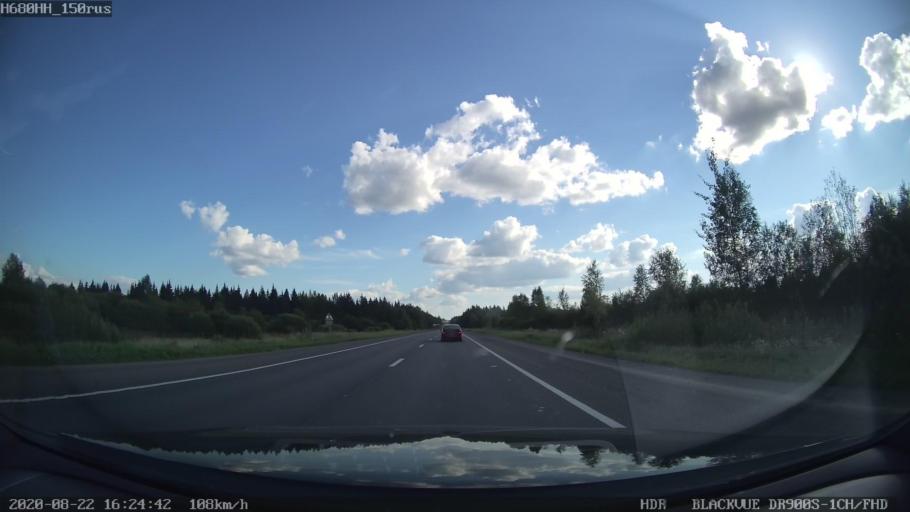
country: RU
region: Tverskaya
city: Rameshki
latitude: 57.3326
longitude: 36.0940
